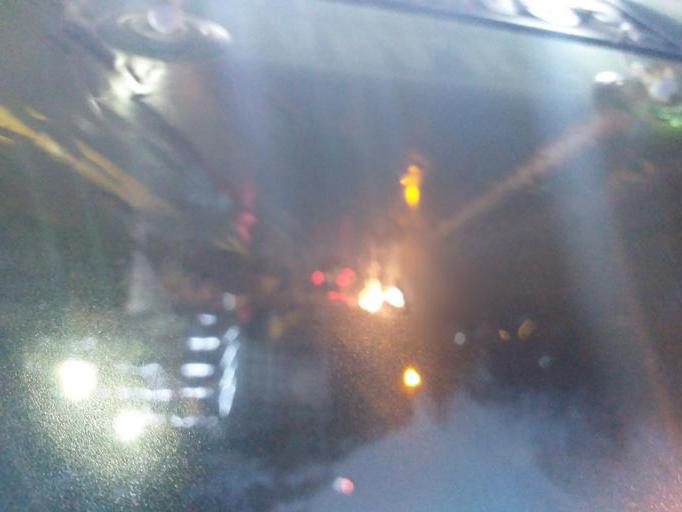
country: TR
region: Ankara
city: Ankara
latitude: 39.9400
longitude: 32.8245
